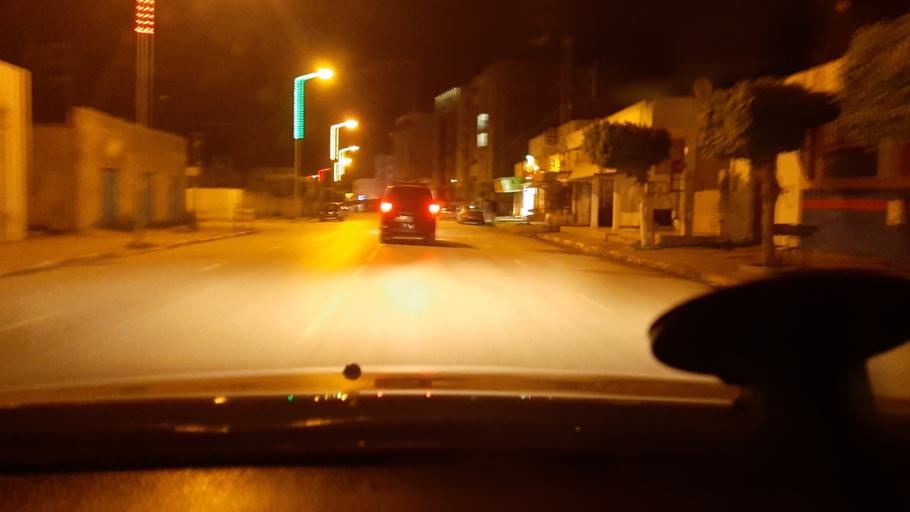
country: TN
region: Safaqis
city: Sfax
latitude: 34.7825
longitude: 10.7228
